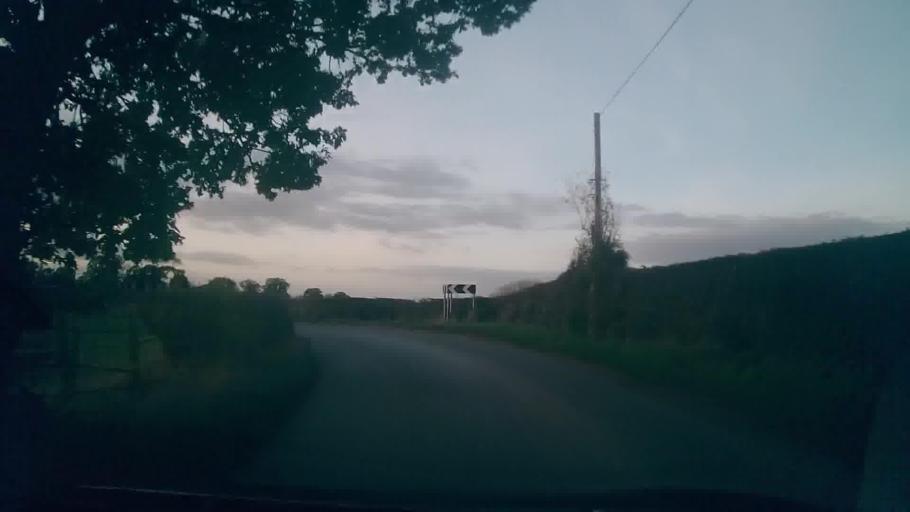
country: GB
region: England
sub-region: Shropshire
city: Clive
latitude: 52.8250
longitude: -2.7268
